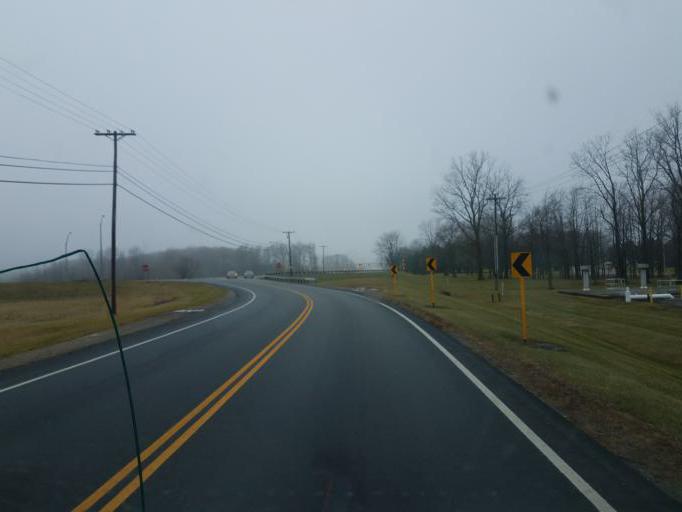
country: US
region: Ohio
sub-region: Champaign County
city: North Lewisburg
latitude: 40.2709
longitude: -83.4958
